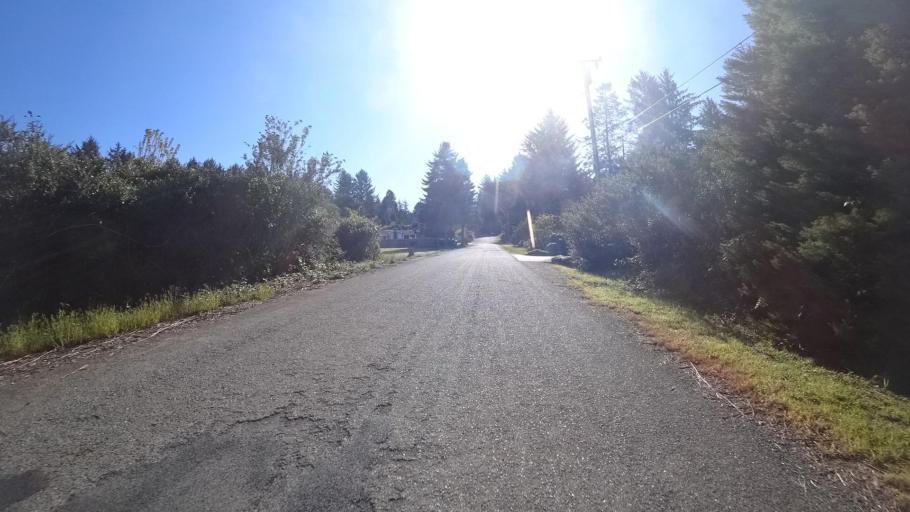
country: US
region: California
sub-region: Humboldt County
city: McKinleyville
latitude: 40.9634
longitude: -124.0942
